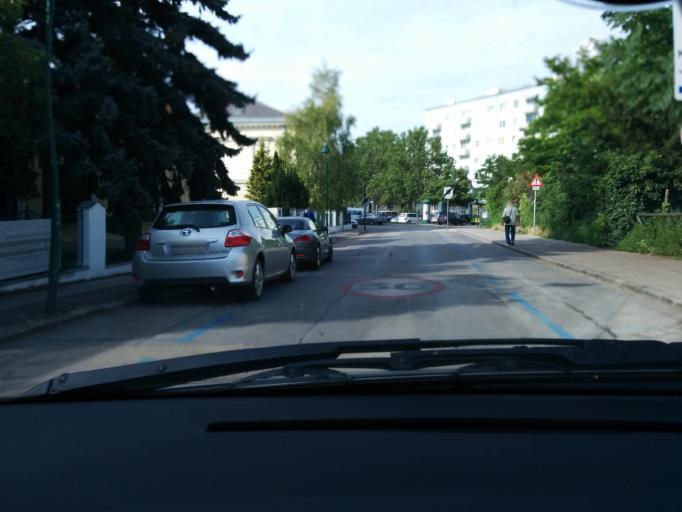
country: AT
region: Lower Austria
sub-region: Politischer Bezirk Modling
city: Modling
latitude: 48.0871
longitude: 16.2851
